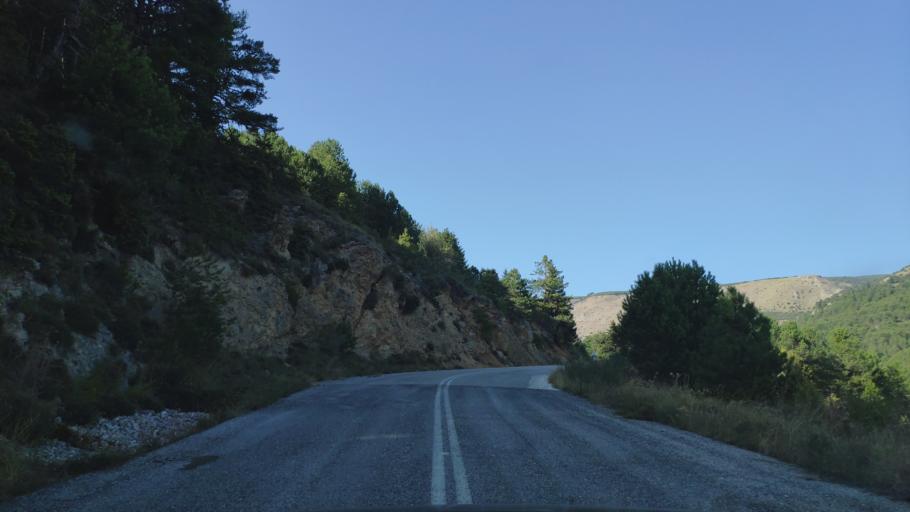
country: GR
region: West Greece
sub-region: Nomos Achaias
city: Aiyira
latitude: 38.0160
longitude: 22.4045
